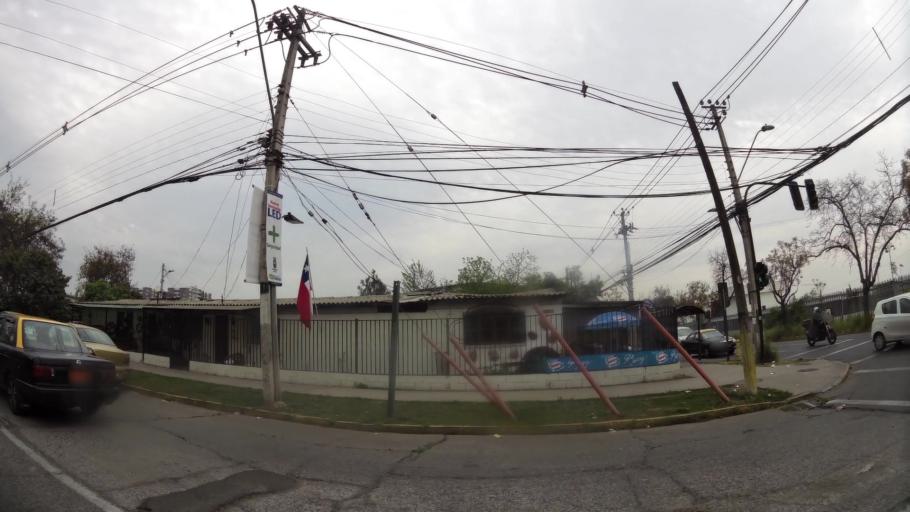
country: CL
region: Santiago Metropolitan
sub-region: Provincia de Santiago
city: Villa Presidente Frei, Nunoa, Santiago, Chile
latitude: -33.4687
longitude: -70.6065
